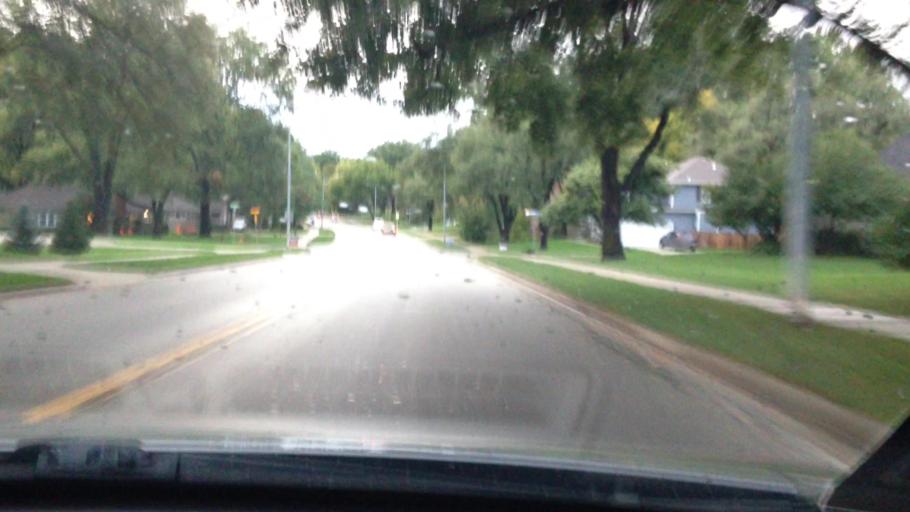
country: US
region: Kansas
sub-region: Johnson County
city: Prairie Village
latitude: 38.9842
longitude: -94.6183
